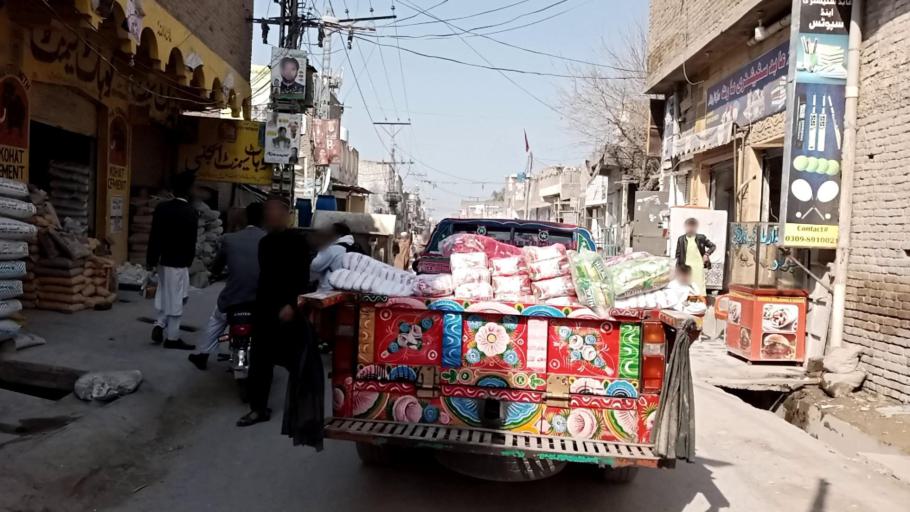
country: PK
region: Khyber Pakhtunkhwa
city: Peshawar
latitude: 34.0114
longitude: 71.5157
